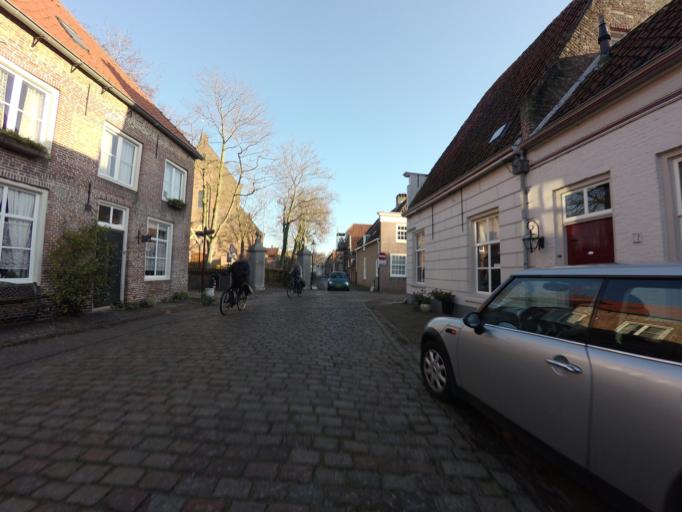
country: NL
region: North Brabant
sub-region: Gemeente Heusden
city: Heusden
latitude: 51.7332
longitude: 5.1372
